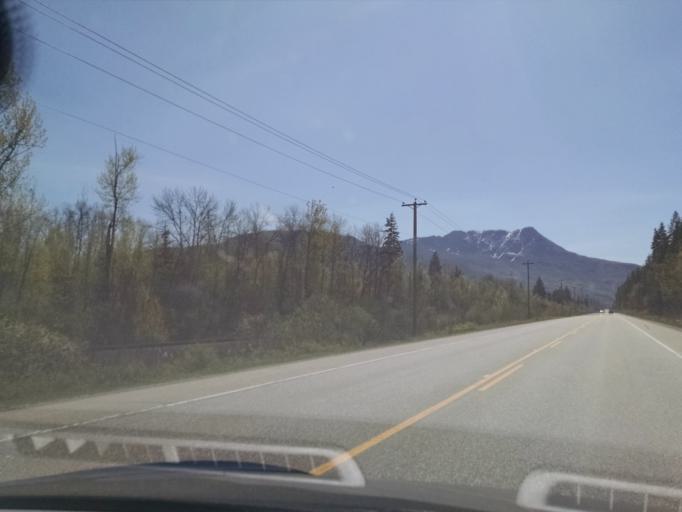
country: CA
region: British Columbia
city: Salmon Arm
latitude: 50.7283
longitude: -119.3160
